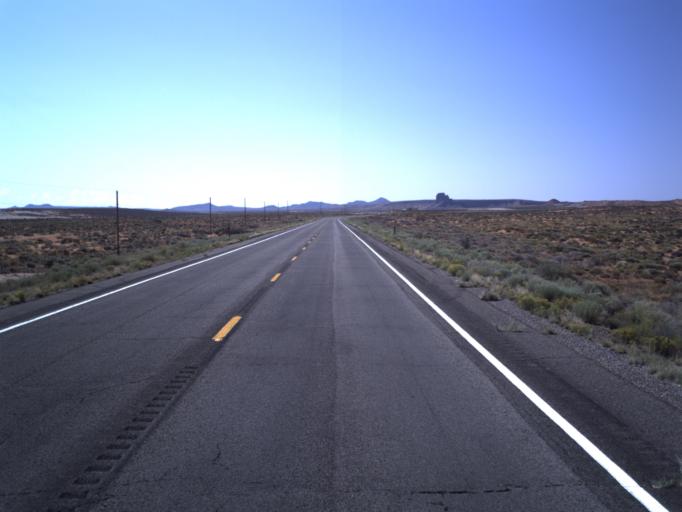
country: US
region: Utah
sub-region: San Juan County
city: Blanding
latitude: 37.0838
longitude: -109.5480
